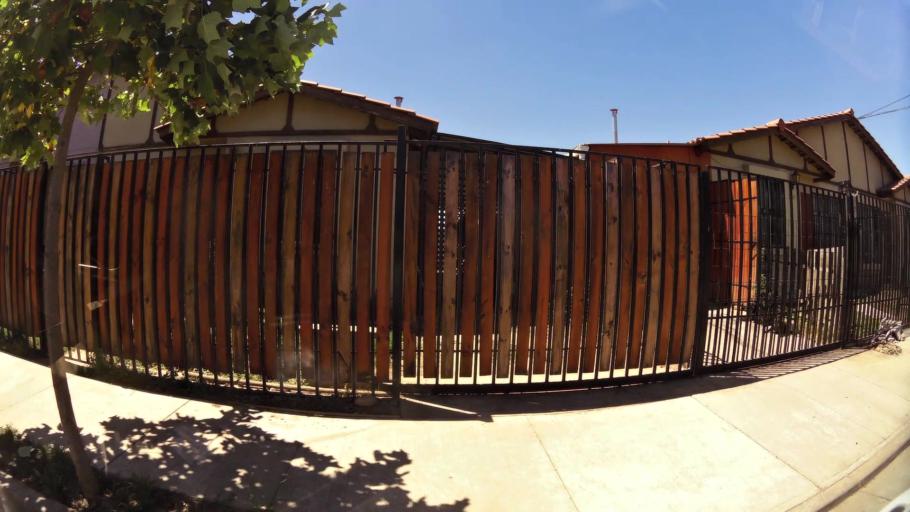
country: CL
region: O'Higgins
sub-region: Provincia de Cachapoal
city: Rancagua
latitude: -34.1507
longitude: -70.7648
